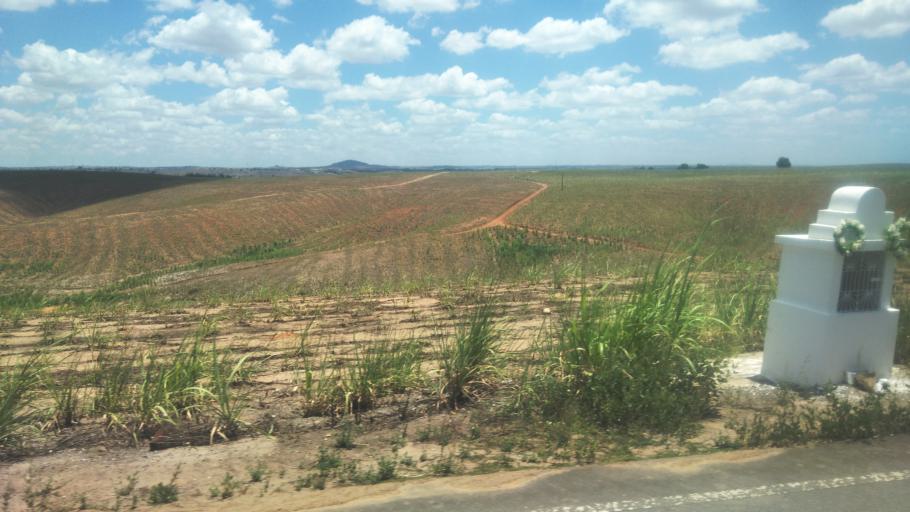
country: BR
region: Pernambuco
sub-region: Nazare Da Mata
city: Nazare da Mata
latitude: -7.7320
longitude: -35.2496
